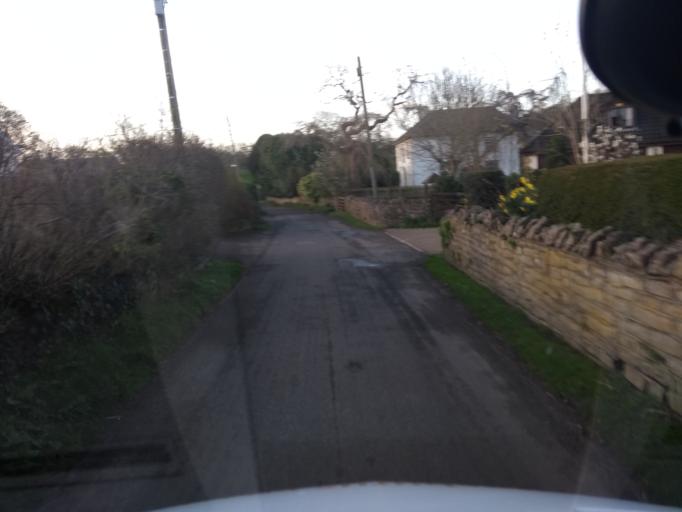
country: GB
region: England
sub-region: Somerset
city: Wedmore
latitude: 51.2258
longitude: -2.8427
